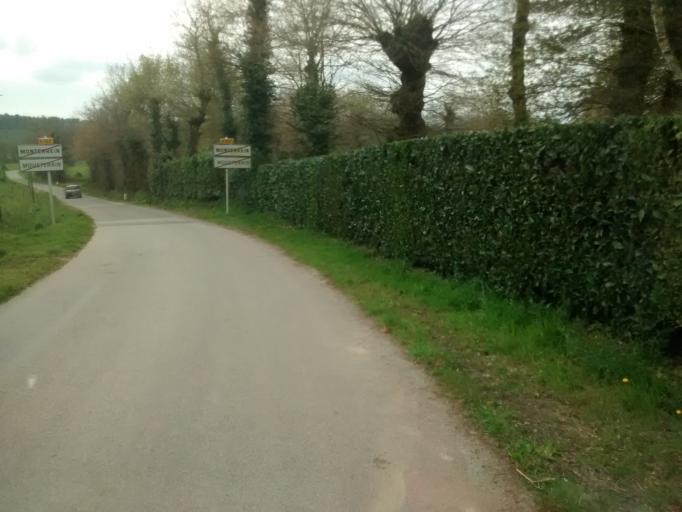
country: FR
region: Brittany
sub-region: Departement du Morbihan
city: Caro
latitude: 47.8789
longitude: -2.3598
